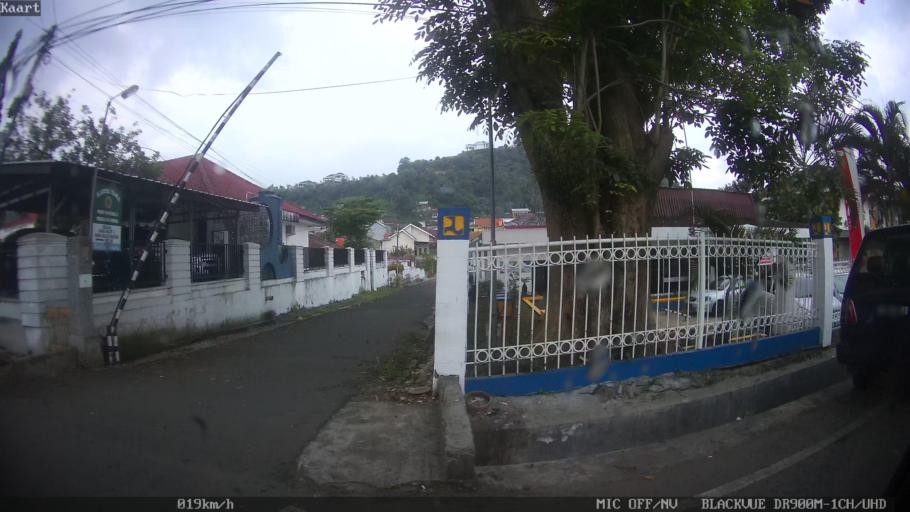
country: ID
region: Lampung
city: Bandarlampung
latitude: -5.4359
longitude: 105.2856
